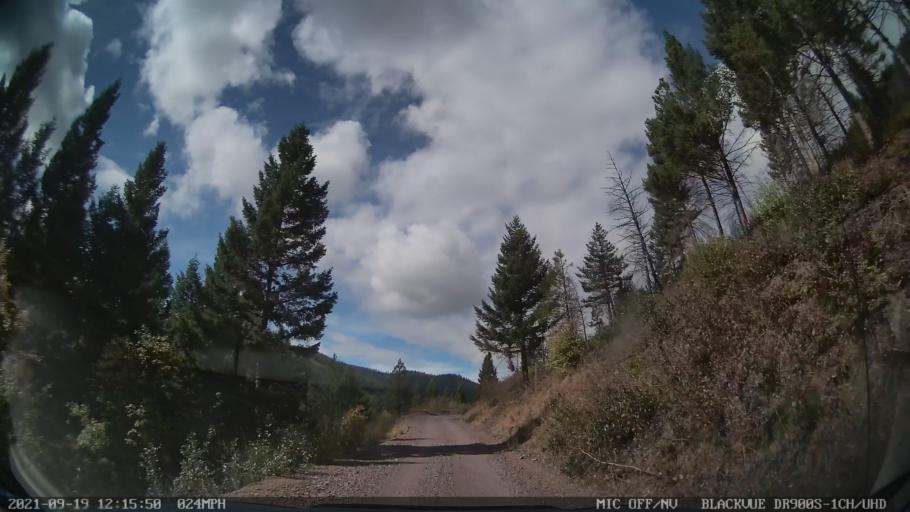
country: US
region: Montana
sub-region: Missoula County
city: Seeley Lake
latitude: 47.1682
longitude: -113.3467
